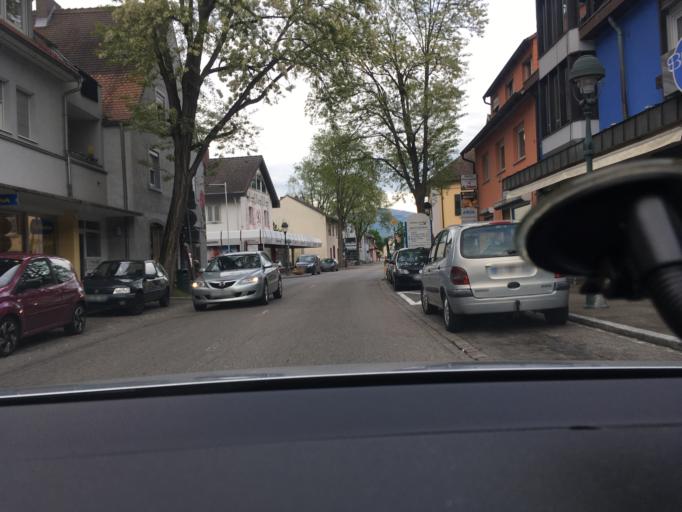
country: DE
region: Baden-Wuerttemberg
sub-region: Freiburg Region
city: Neuenburg am Rhein
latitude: 47.8137
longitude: 7.5615
